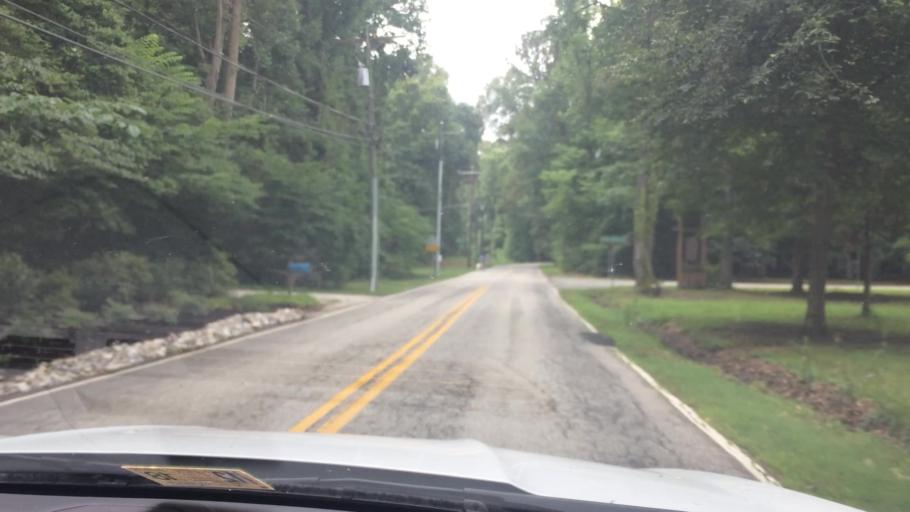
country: US
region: Virginia
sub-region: City of Williamsburg
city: Williamsburg
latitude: 37.2819
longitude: -76.6720
